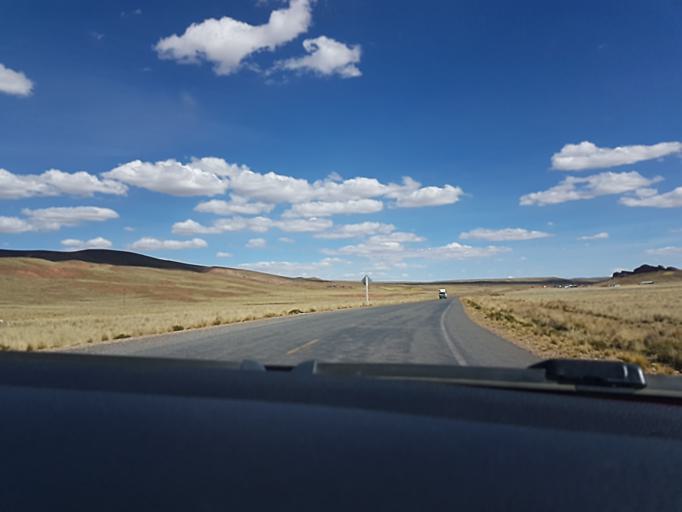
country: BO
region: La Paz
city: Tiahuanaco
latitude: -17.0156
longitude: -68.4292
